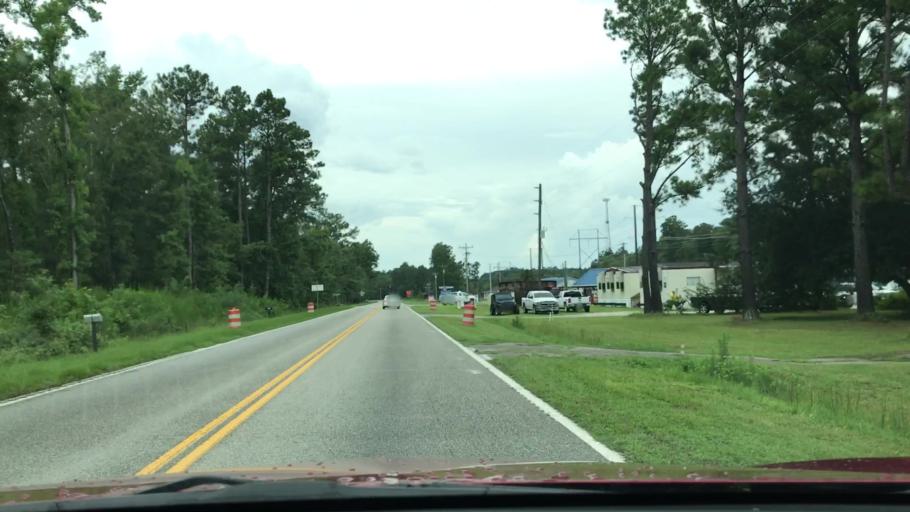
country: US
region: South Carolina
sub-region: Georgetown County
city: Murrells Inlet
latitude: 33.6520
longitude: -79.1664
